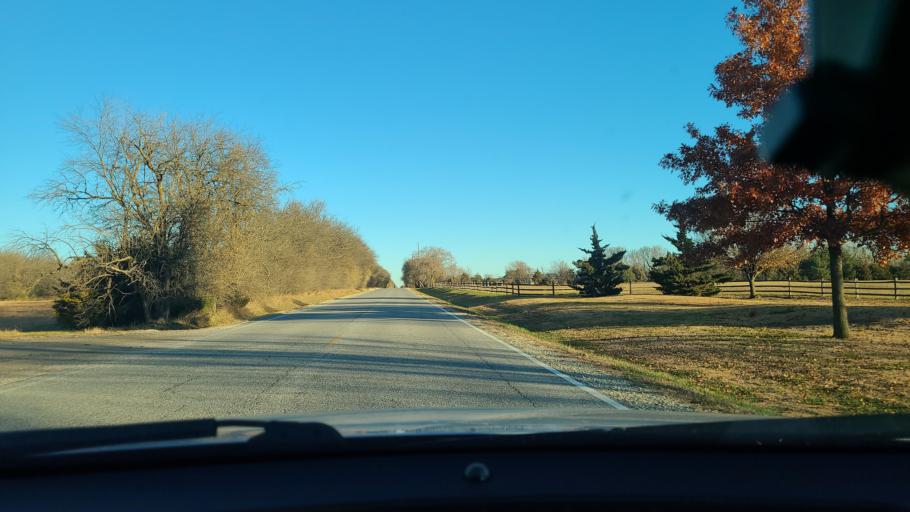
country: US
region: Kansas
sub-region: Sedgwick County
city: Park City
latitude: 37.8481
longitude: -97.3174
